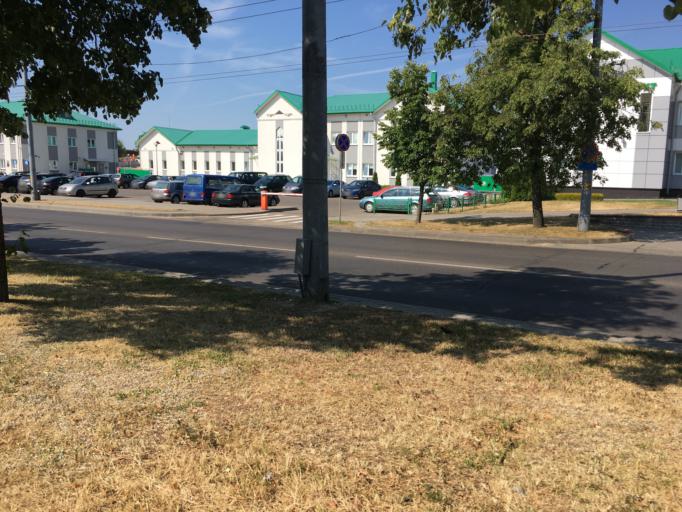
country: BY
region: Grodnenskaya
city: Hrodna
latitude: 53.7093
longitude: 23.8401
